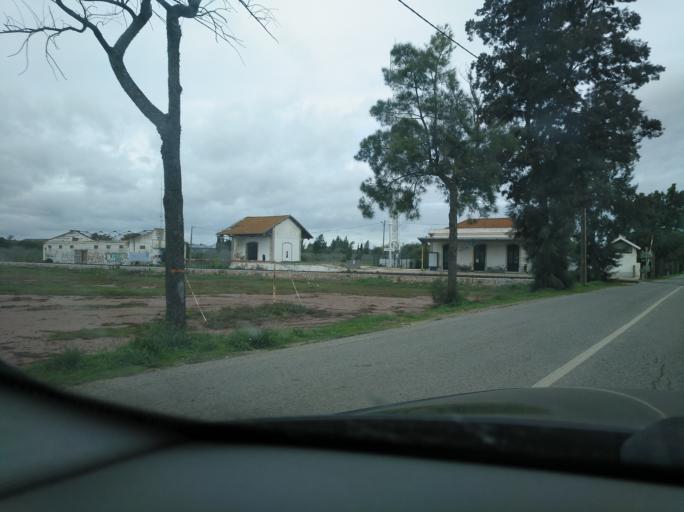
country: PT
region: Faro
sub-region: Vila Real de Santo Antonio
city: Monte Gordo
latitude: 37.1962
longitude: -7.4839
